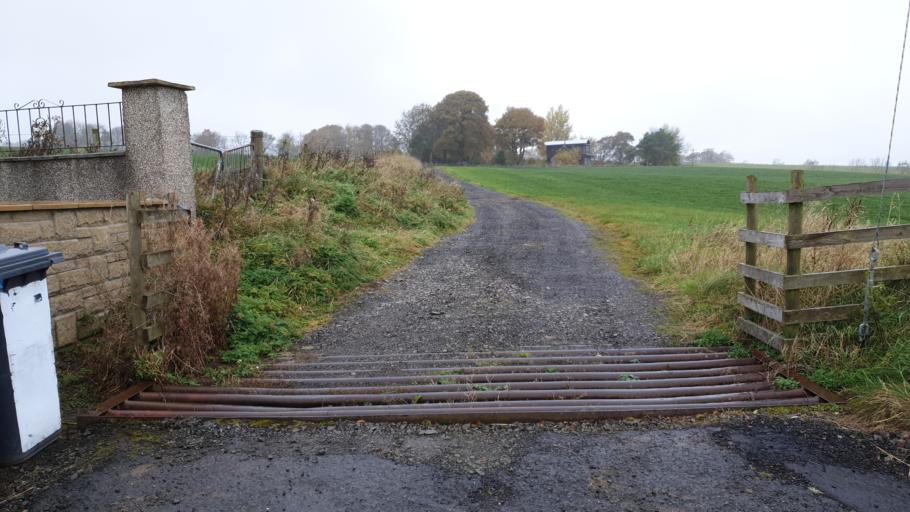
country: GB
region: Scotland
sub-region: South Lanarkshire
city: Lesmahagow
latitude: 55.6280
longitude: -3.8993
